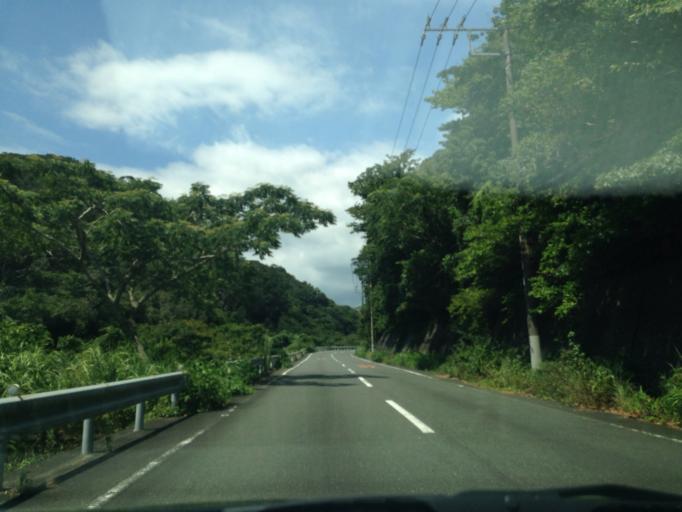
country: JP
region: Shizuoka
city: Shimoda
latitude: 34.6229
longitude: 138.8239
